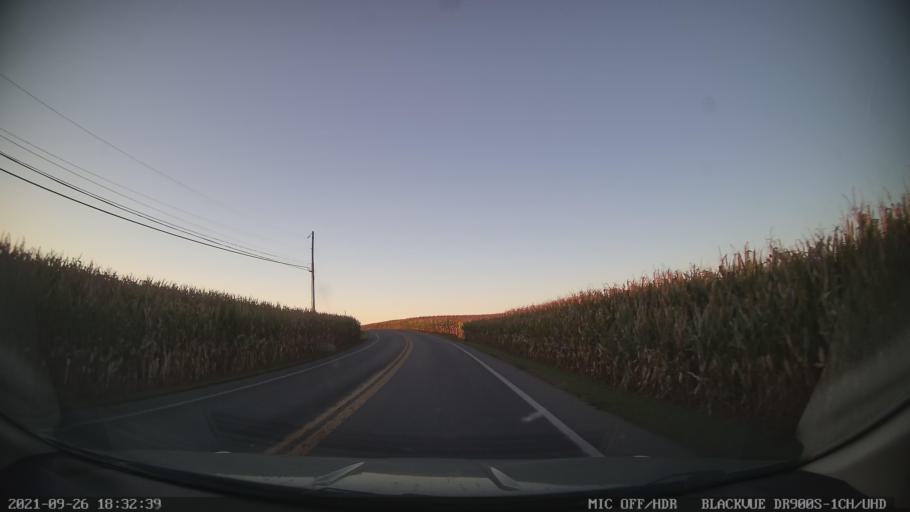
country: US
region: Pennsylvania
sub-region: Berks County
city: Kutztown
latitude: 40.4924
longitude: -75.7611
